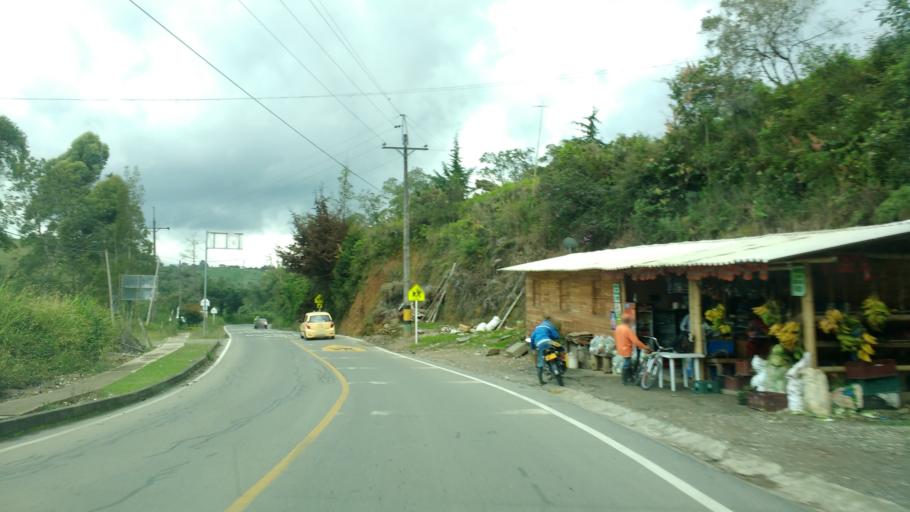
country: CO
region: Antioquia
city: Marinilla
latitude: 6.1861
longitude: -75.2928
